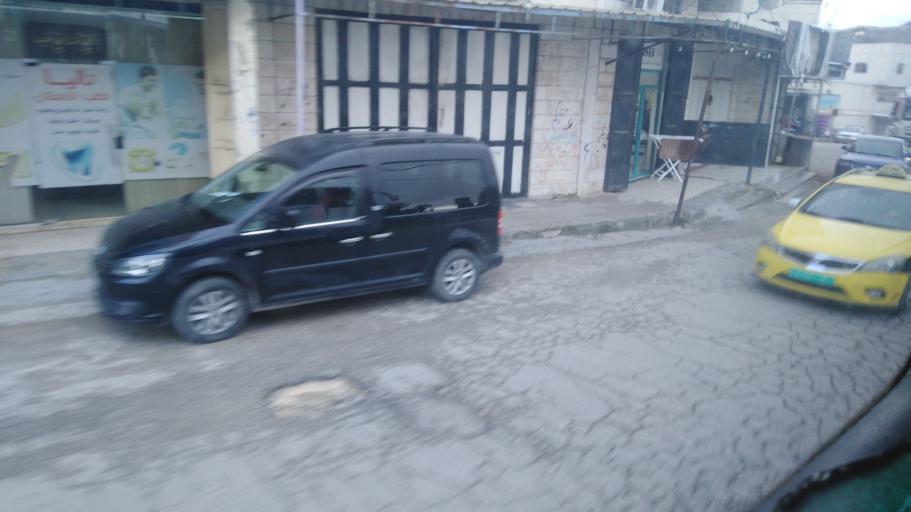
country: PS
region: West Bank
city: Hebron
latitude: 31.5292
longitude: 35.0793
